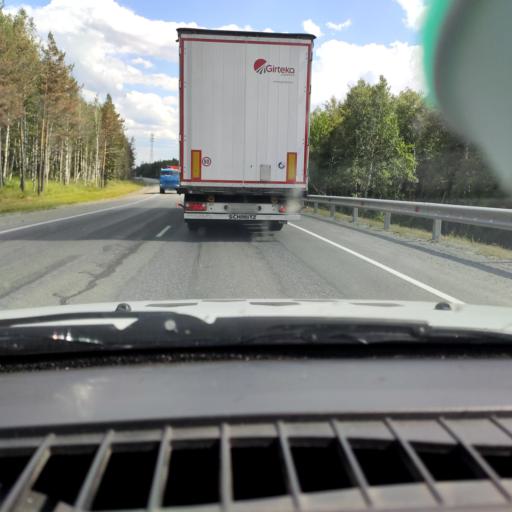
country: RU
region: Chelyabinsk
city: Zlatoust
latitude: 55.0226
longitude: 59.7267
